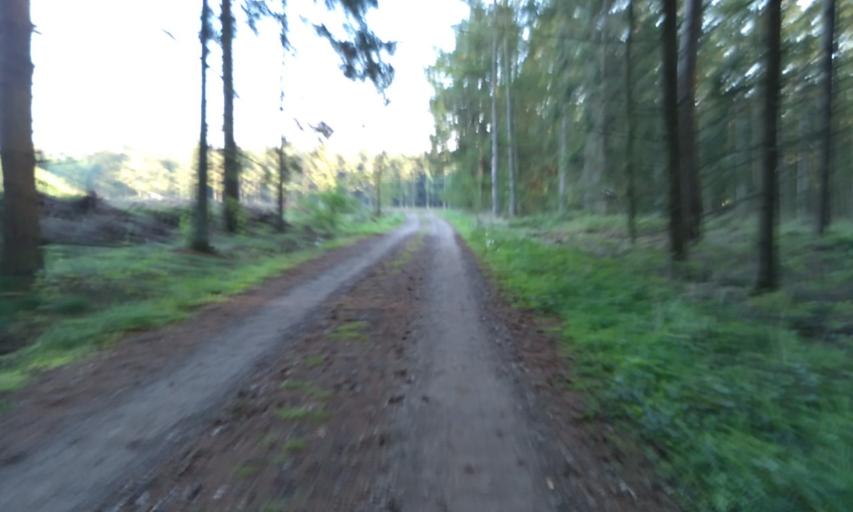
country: DE
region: Lower Saxony
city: Dollern
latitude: 53.5216
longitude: 9.5383
